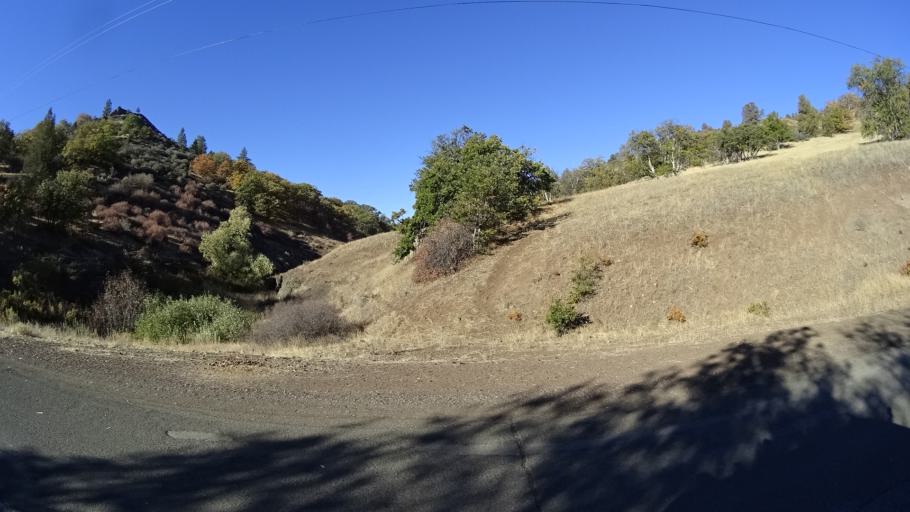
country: US
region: California
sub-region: Siskiyou County
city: Montague
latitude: 41.9696
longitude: -122.4402
